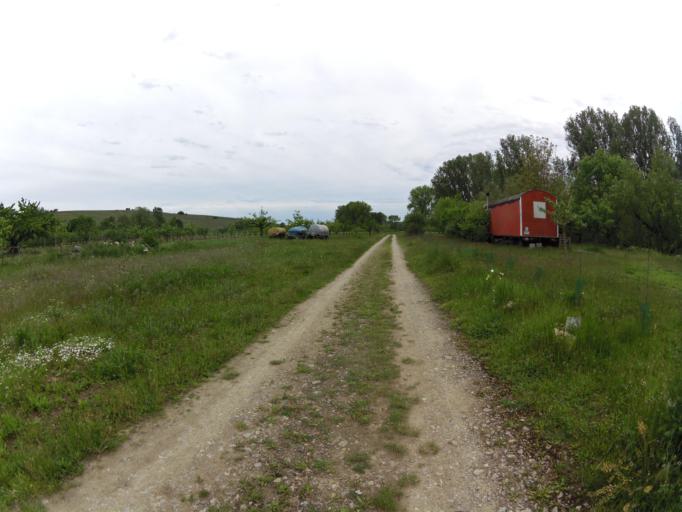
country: DE
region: Bavaria
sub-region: Regierungsbezirk Unterfranken
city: Nordheim
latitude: 49.8454
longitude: 10.1727
